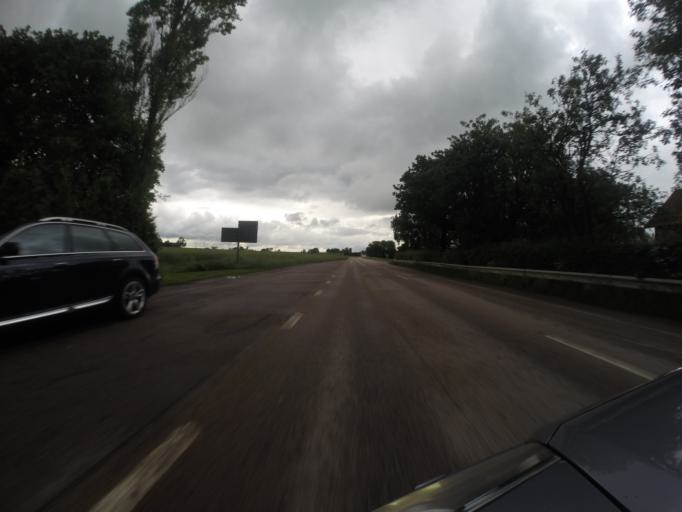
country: SE
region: Skane
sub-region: Landskrona
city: Asmundtorp
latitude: 55.9552
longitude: 12.9462
